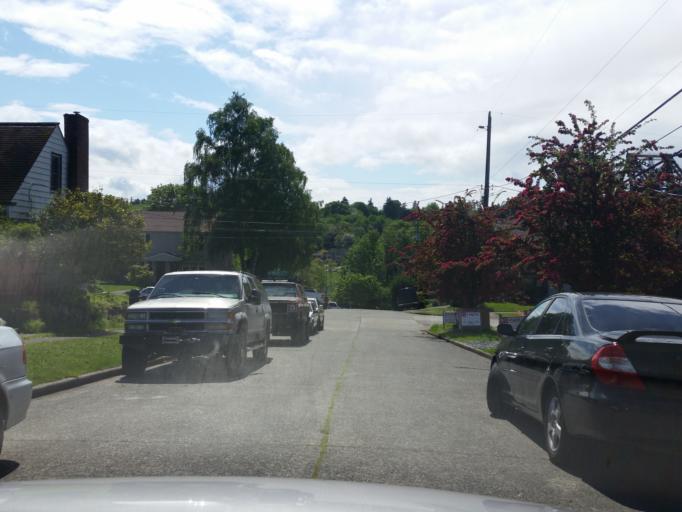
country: US
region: Washington
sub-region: King County
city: Seattle
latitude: 47.6691
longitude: -122.4012
